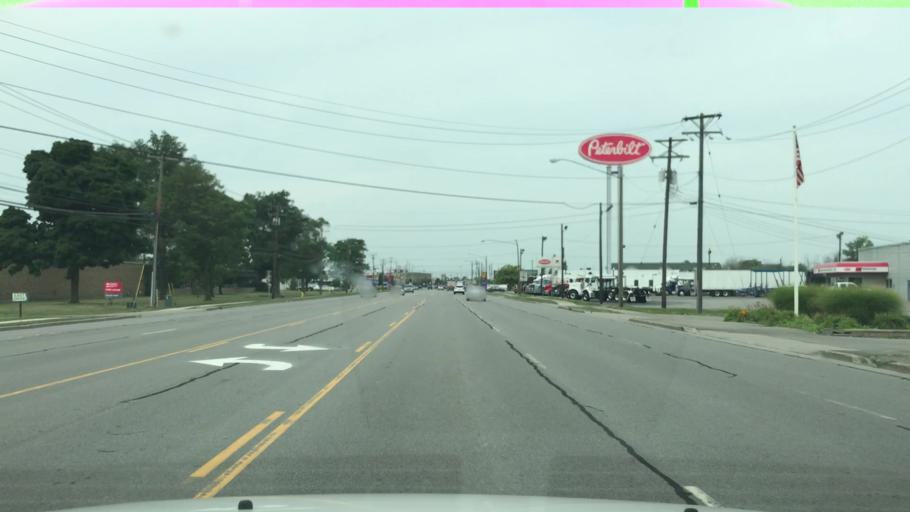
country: US
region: New York
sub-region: Erie County
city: Cheektowaga
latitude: 42.9079
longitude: -78.7475
